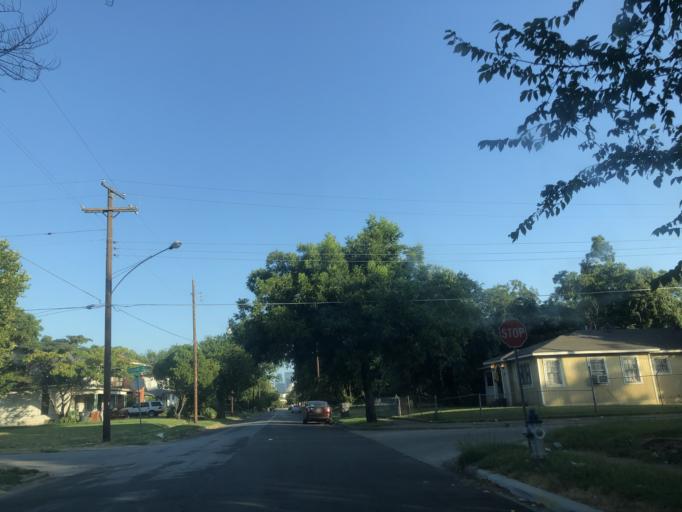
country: US
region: Texas
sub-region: Dallas County
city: Dallas
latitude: 32.7582
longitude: -96.7708
